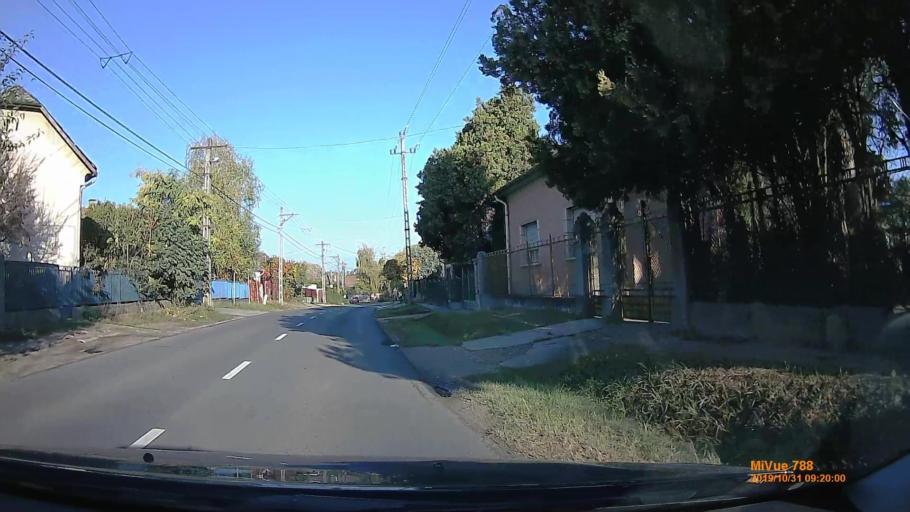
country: HU
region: Pest
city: Gyomro
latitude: 47.4208
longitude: 19.3881
